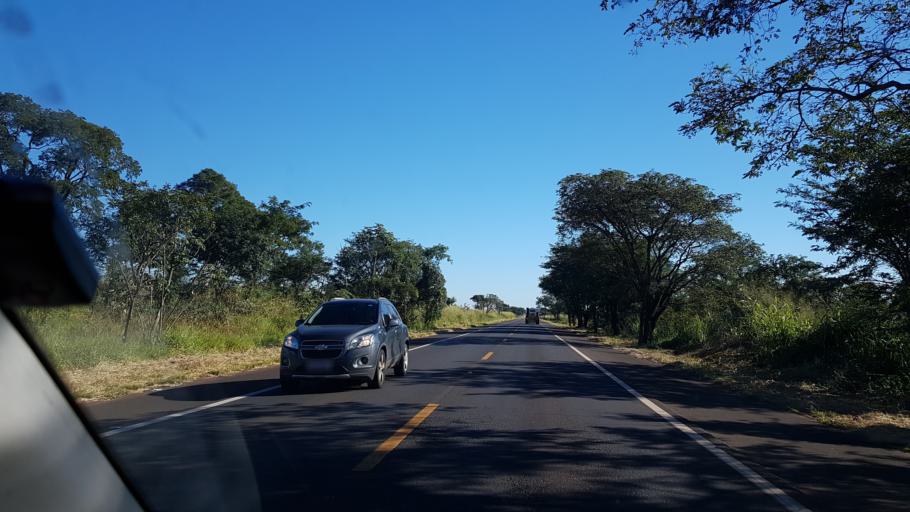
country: BR
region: Sao Paulo
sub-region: Maracai
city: Maracai
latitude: -22.5574
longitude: -50.5278
